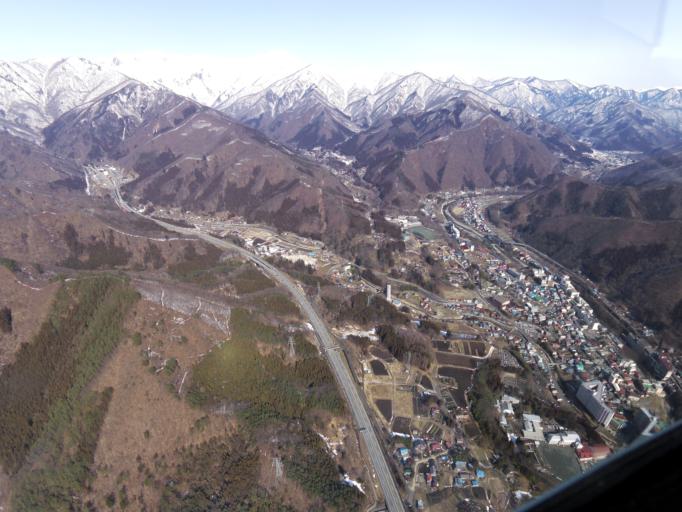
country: JP
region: Gunma
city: Numata
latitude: 36.7624
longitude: 138.9645
